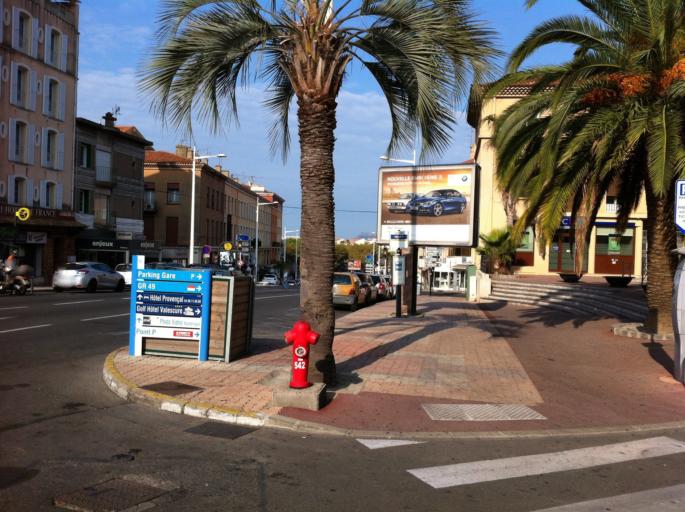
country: FR
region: Provence-Alpes-Cote d'Azur
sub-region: Departement du Var
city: Saint-Raphael
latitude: 43.4239
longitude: 6.7684
